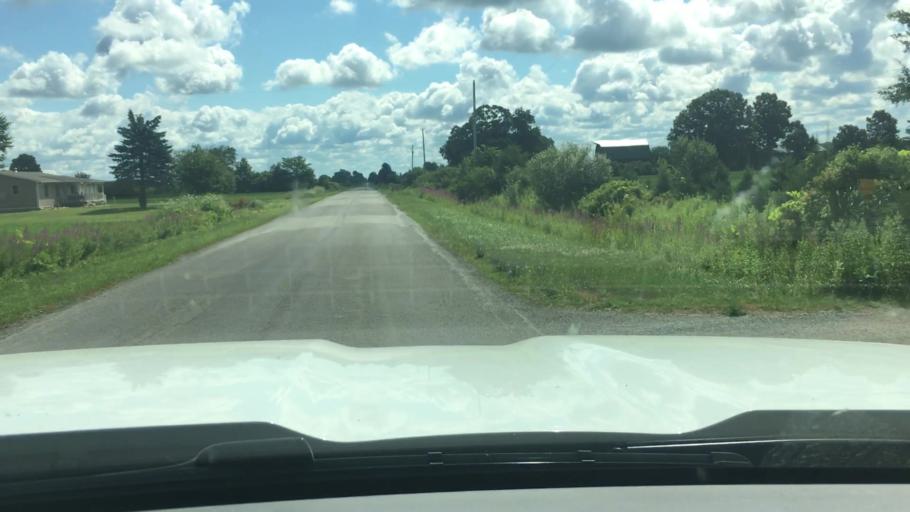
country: US
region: Michigan
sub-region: Saginaw County
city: Chesaning
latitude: 43.2157
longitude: -84.1622
